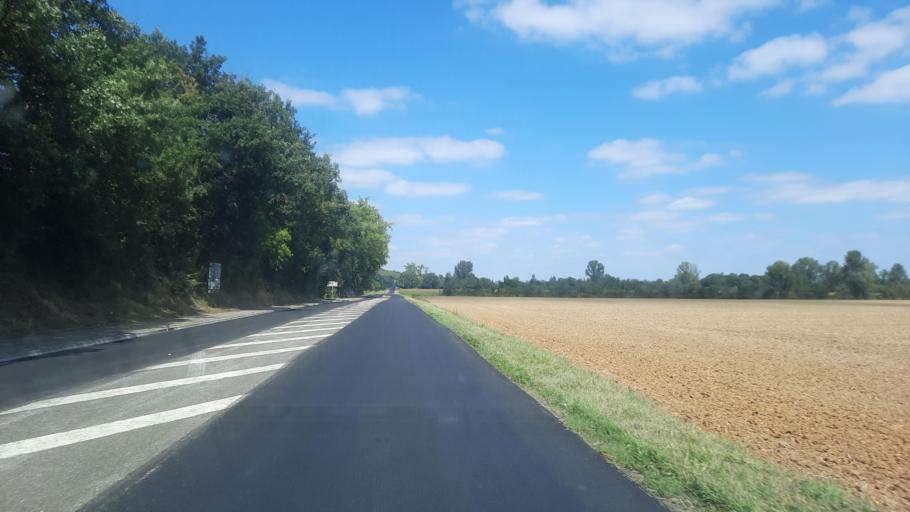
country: FR
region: Midi-Pyrenees
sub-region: Departement du Gers
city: Lombez
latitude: 43.4605
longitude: 0.8853
